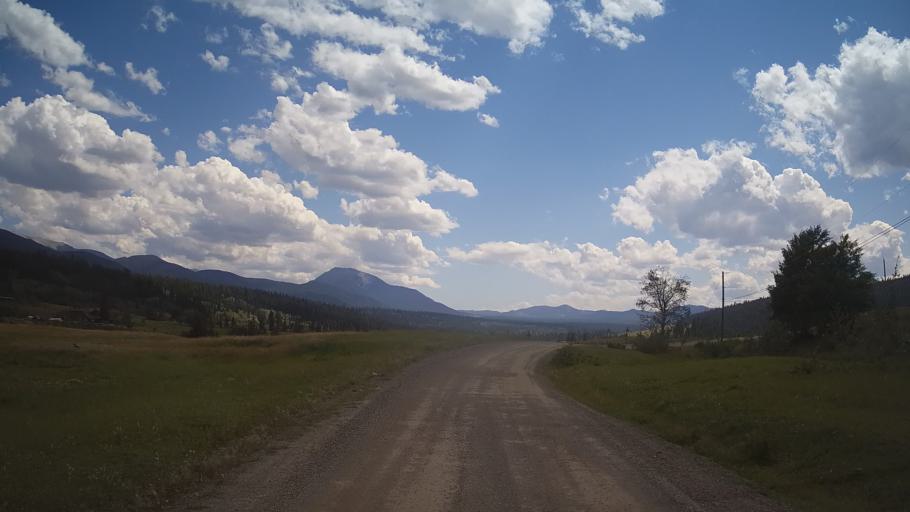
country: CA
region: British Columbia
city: Lillooet
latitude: 51.3107
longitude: -121.9845
